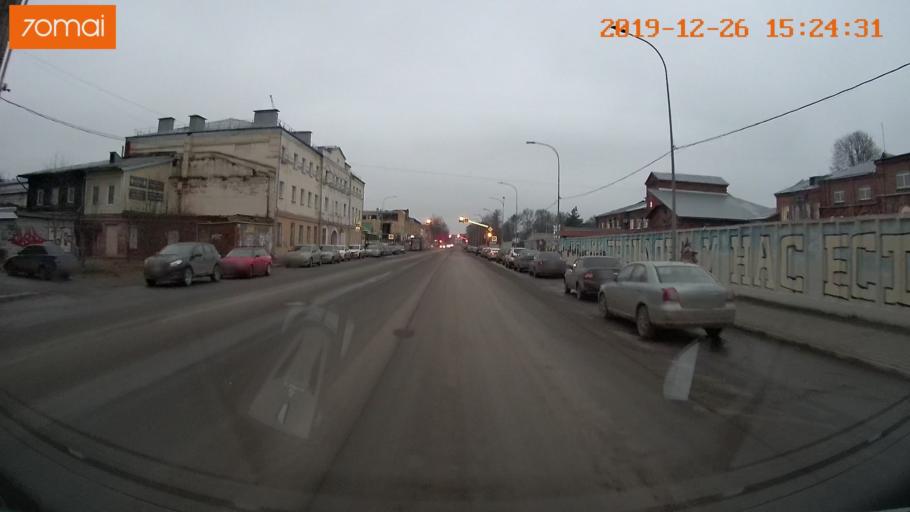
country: RU
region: Jaroslavl
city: Rybinsk
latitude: 58.0509
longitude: 38.8483
